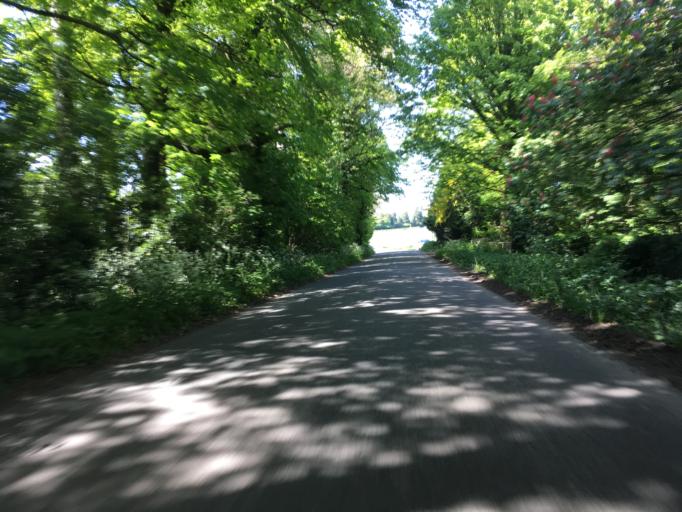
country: GB
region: England
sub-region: Gloucestershire
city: Coates
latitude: 51.6992
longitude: -2.0241
